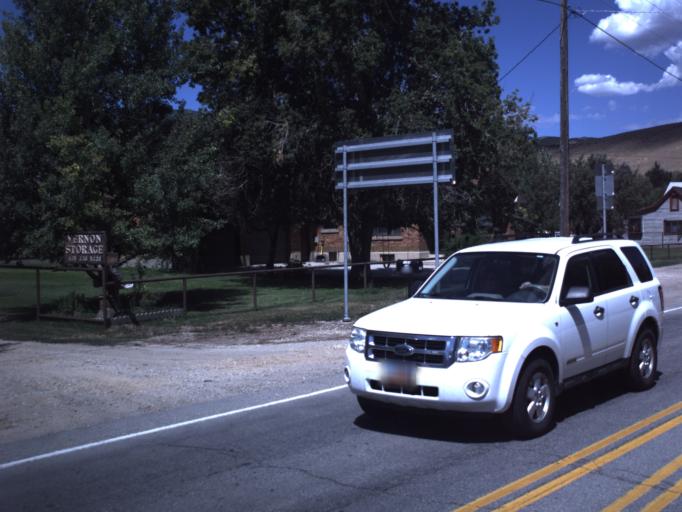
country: US
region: Utah
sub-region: Summit County
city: Coalville
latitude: 40.8097
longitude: -111.4076
